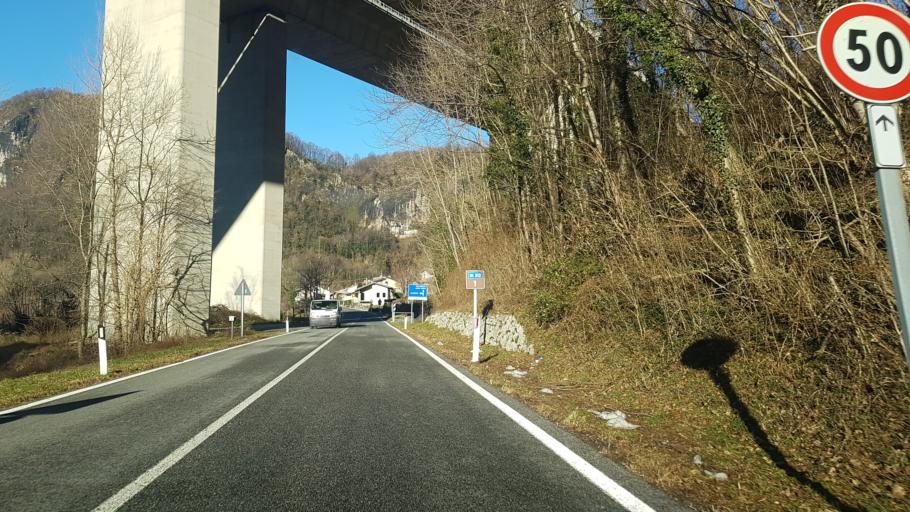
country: IT
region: Friuli Venezia Giulia
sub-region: Provincia di Udine
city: Amaro
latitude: 46.3455
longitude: 13.0714
